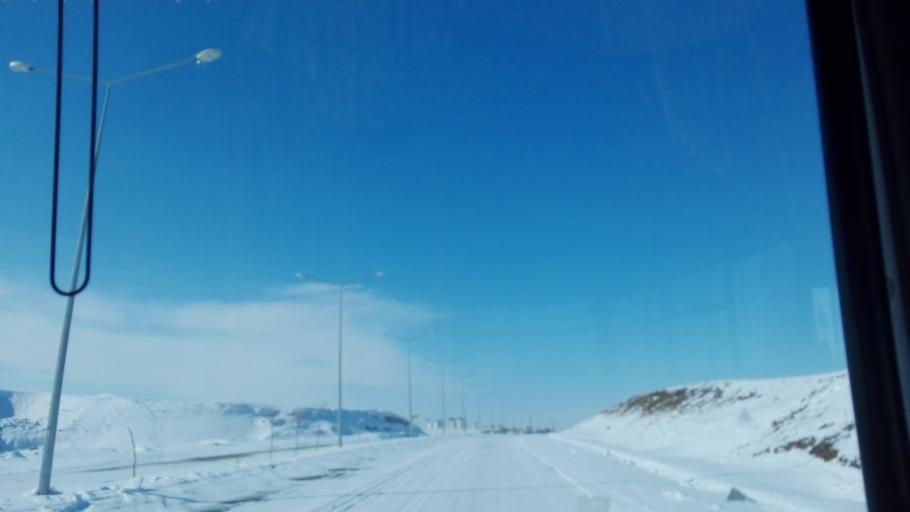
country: TR
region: Batman
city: Erkoklu
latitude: 37.8523
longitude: 41.1133
